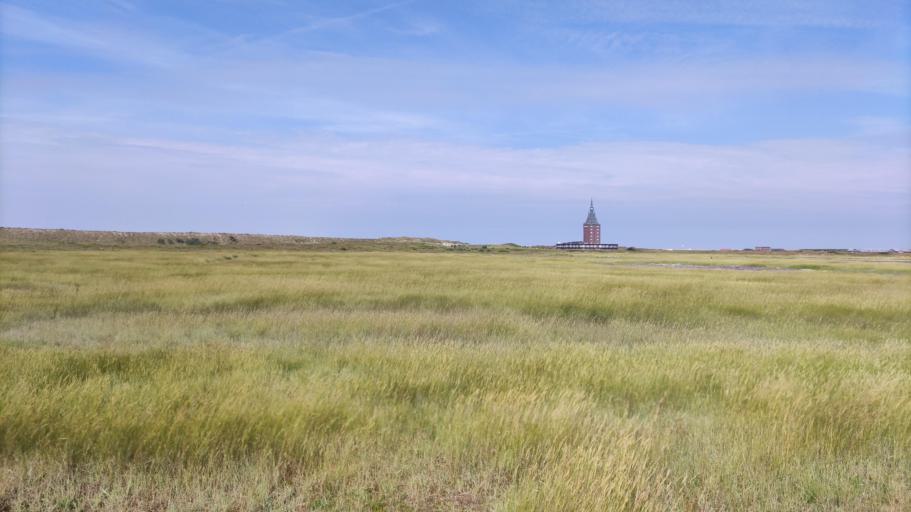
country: DE
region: Lower Saxony
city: Wangerooge
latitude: 53.7825
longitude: 7.8666
